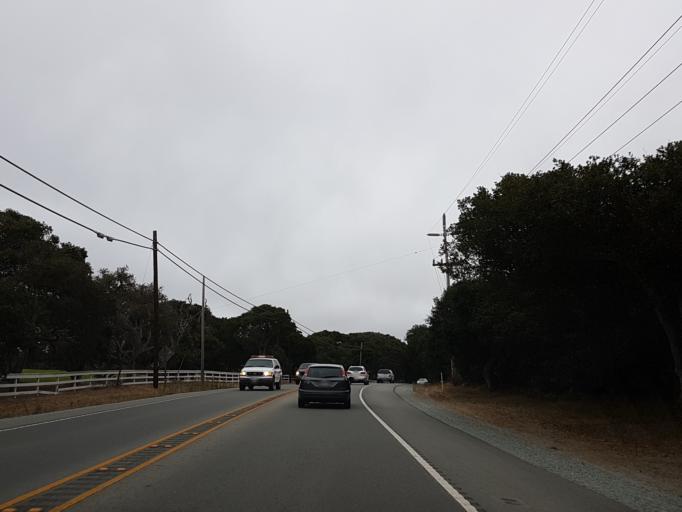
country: US
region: California
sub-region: Monterey County
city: Del Rey Oaks
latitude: 36.5699
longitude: -121.7908
